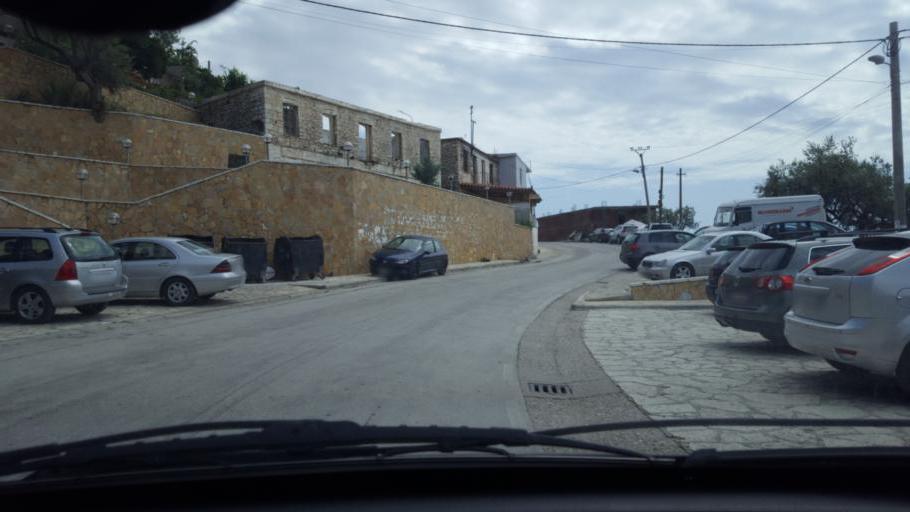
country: AL
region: Vlore
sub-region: Rrethi i Sarandes
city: Lukove
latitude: 40.0616
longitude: 19.8577
